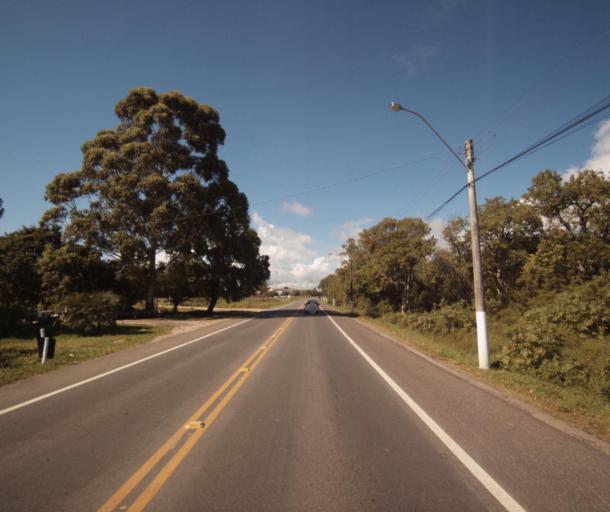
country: BR
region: Rio Grande do Sul
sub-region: Pelotas
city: Pelotas
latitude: -31.7603
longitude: -52.3562
